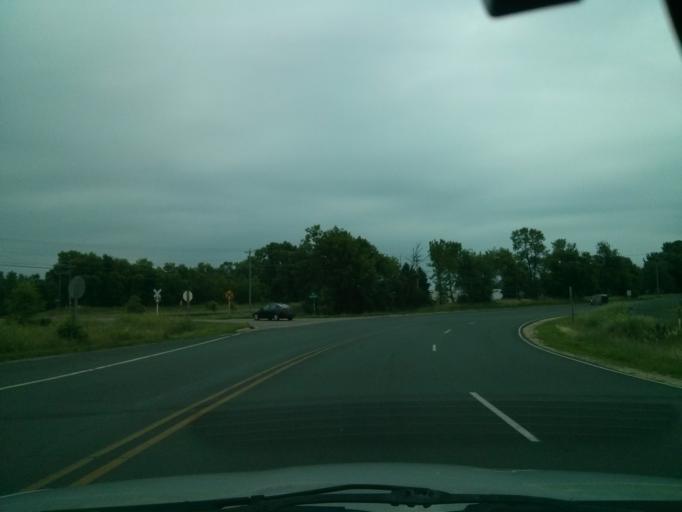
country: US
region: Wisconsin
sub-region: Saint Croix County
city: North Hudson
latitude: 44.9911
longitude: -92.7058
